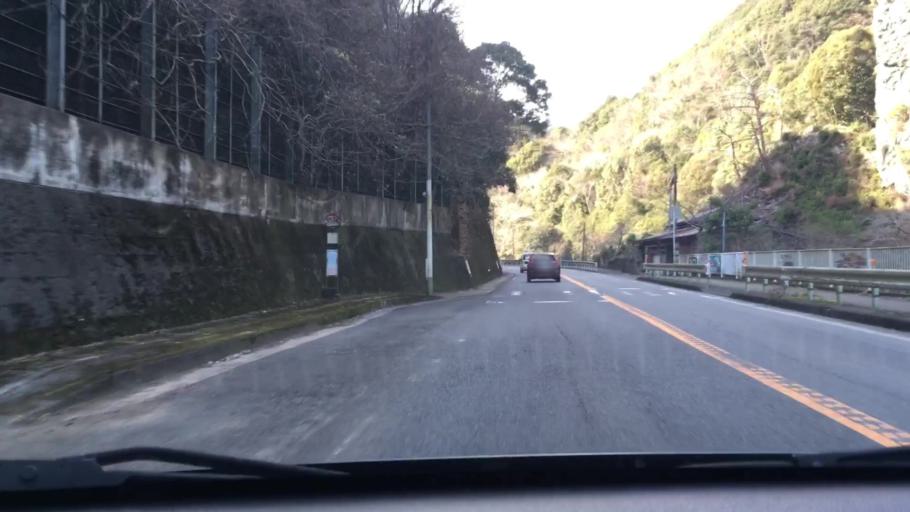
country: JP
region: Oita
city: Tsukumiura
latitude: 33.0039
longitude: 131.7976
